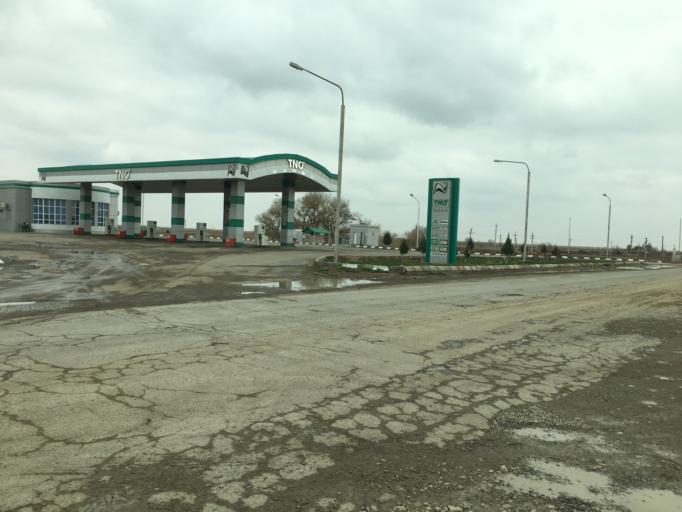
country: TM
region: Ahal
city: Tejen
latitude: 37.3473
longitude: 60.7340
